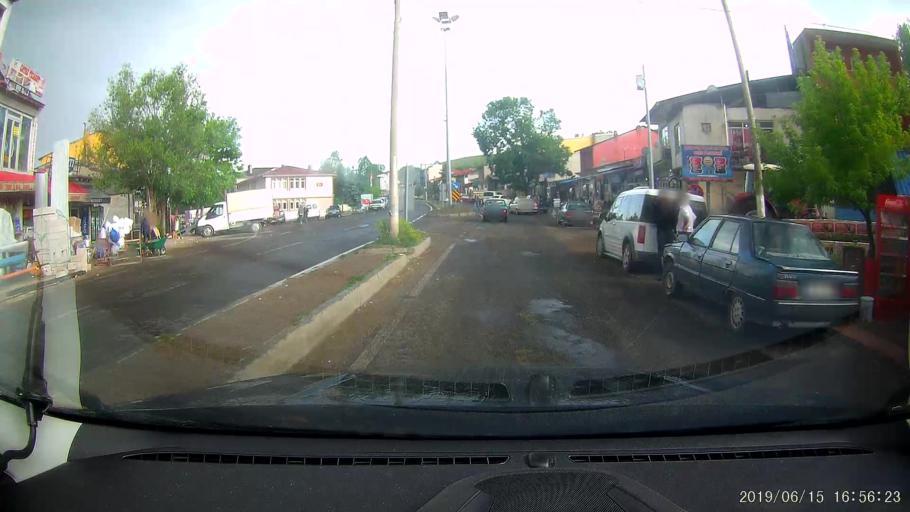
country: TR
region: Kars
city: Susuz
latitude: 40.7802
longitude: 43.1274
